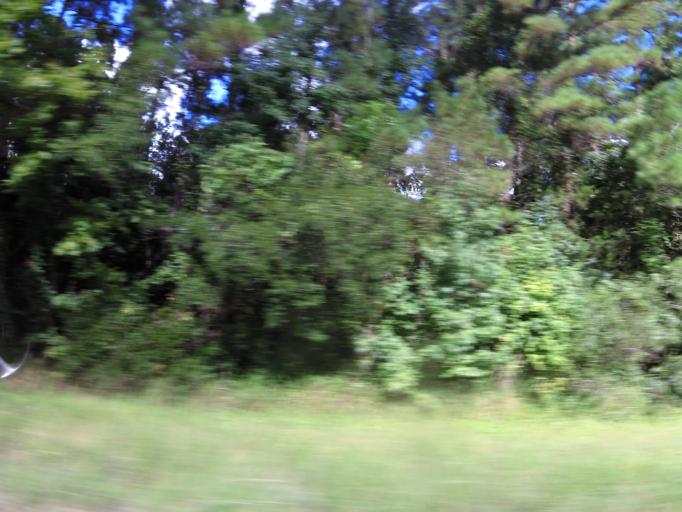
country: US
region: Georgia
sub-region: Camden County
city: Kingsland
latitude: 30.8586
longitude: -81.7019
